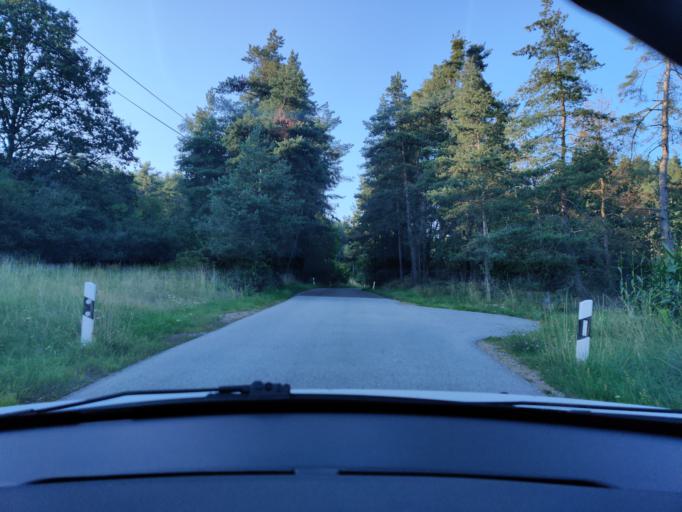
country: DE
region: Bavaria
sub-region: Upper Palatinate
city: Nabburg
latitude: 49.4156
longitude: 12.1772
